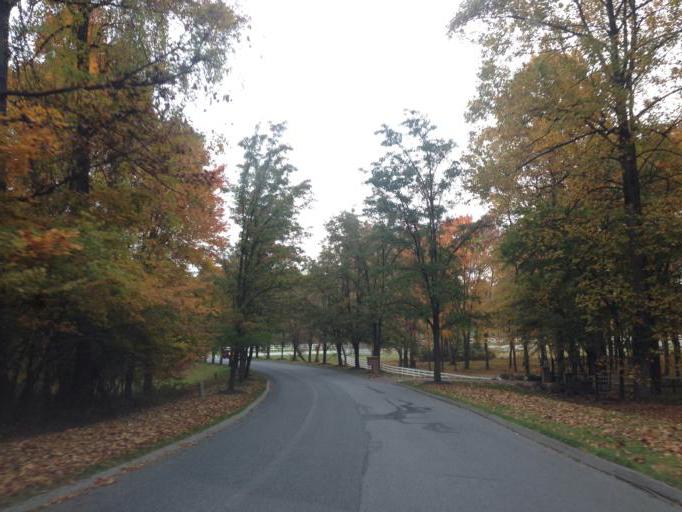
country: US
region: Maryland
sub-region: Howard County
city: Highland
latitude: 39.2561
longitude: -76.9668
